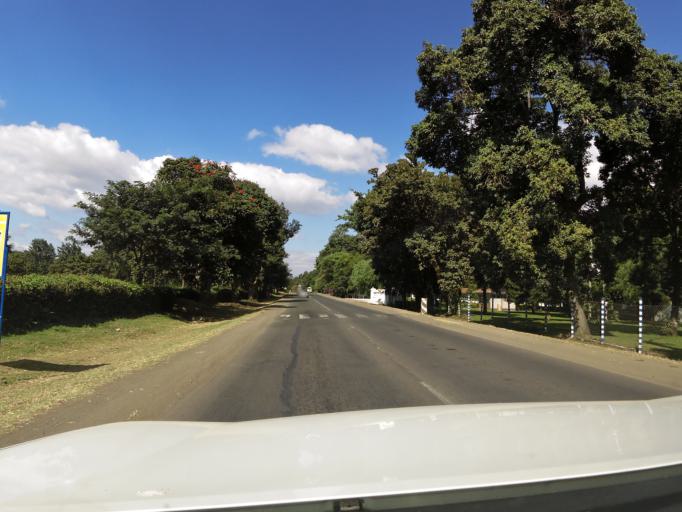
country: TZ
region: Arusha
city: Arusha
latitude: -3.3759
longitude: 36.6488
